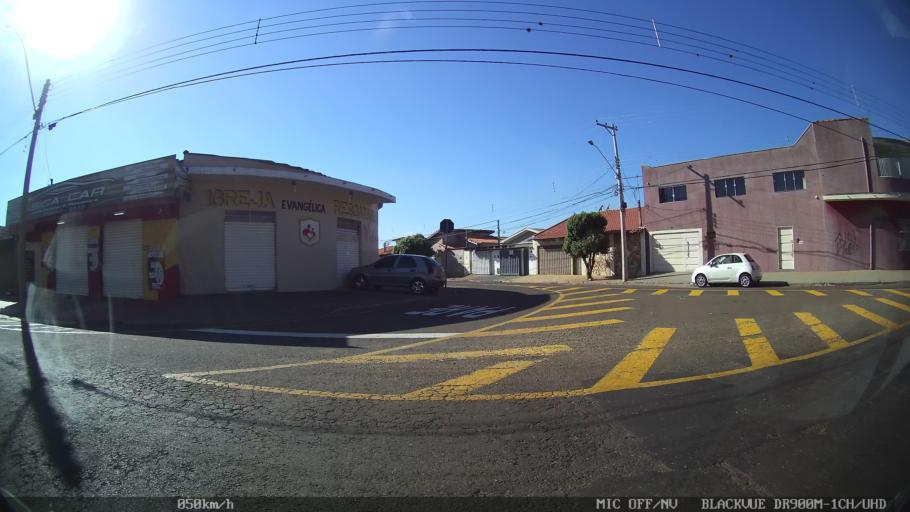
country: BR
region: Sao Paulo
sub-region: Franca
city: Franca
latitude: -20.4873
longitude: -47.4150
